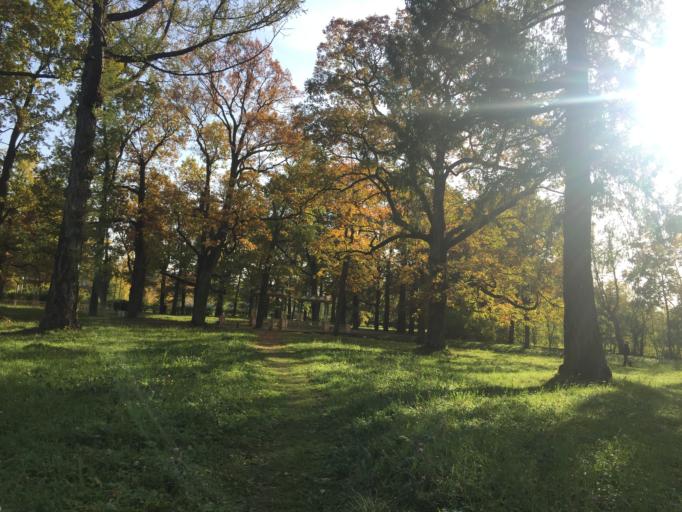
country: RU
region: St.-Petersburg
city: Pushkin
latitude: 59.7171
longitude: 30.3868
